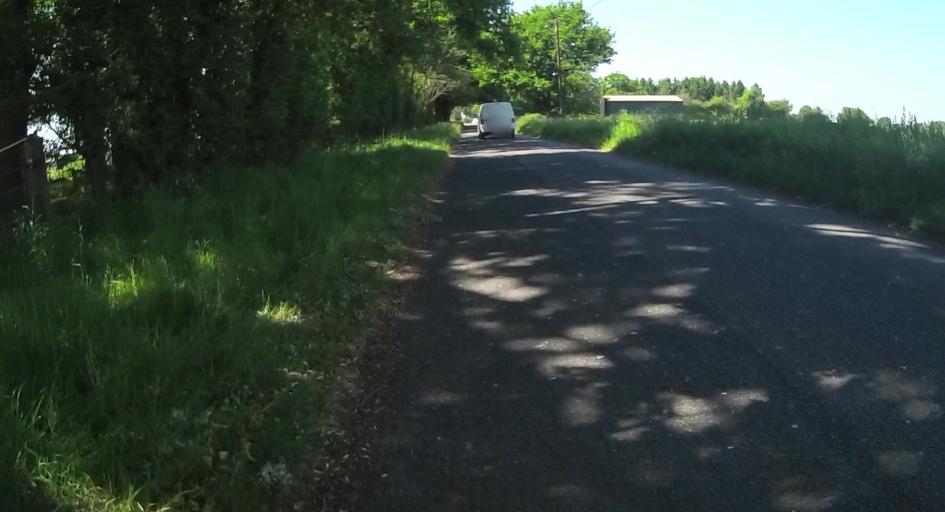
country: GB
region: England
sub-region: Hampshire
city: Kingsclere
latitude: 51.3432
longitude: -1.1981
